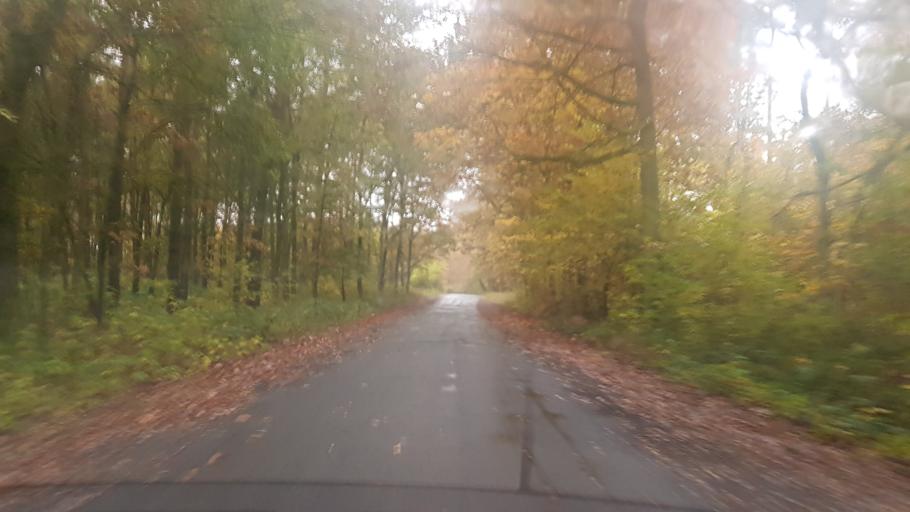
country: PL
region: West Pomeranian Voivodeship
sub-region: Powiat gryfinski
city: Chojna
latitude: 53.0427
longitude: 14.4678
